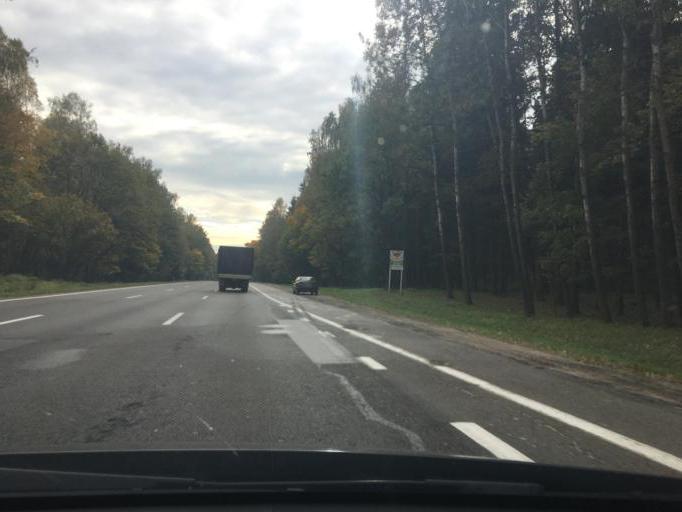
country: BY
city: Fanipol
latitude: 53.7890
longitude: 27.3652
